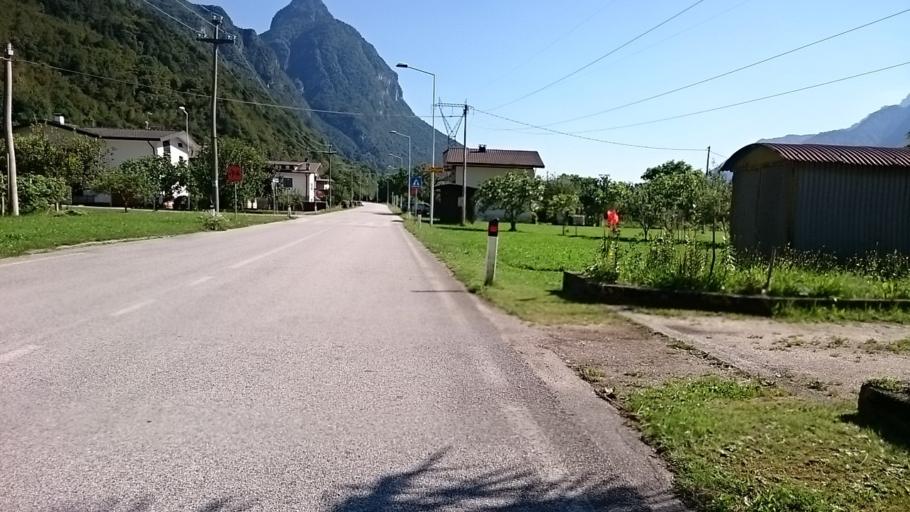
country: IT
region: Veneto
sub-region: Provincia di Belluno
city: Longarone
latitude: 46.2600
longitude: 12.3128
